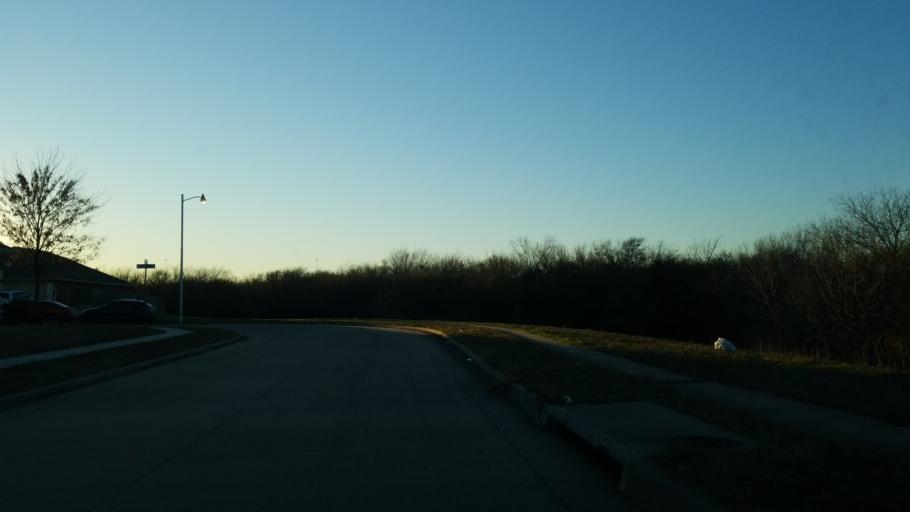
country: US
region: Texas
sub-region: Tarrant County
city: Arlington
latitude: 32.7251
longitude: -97.0544
